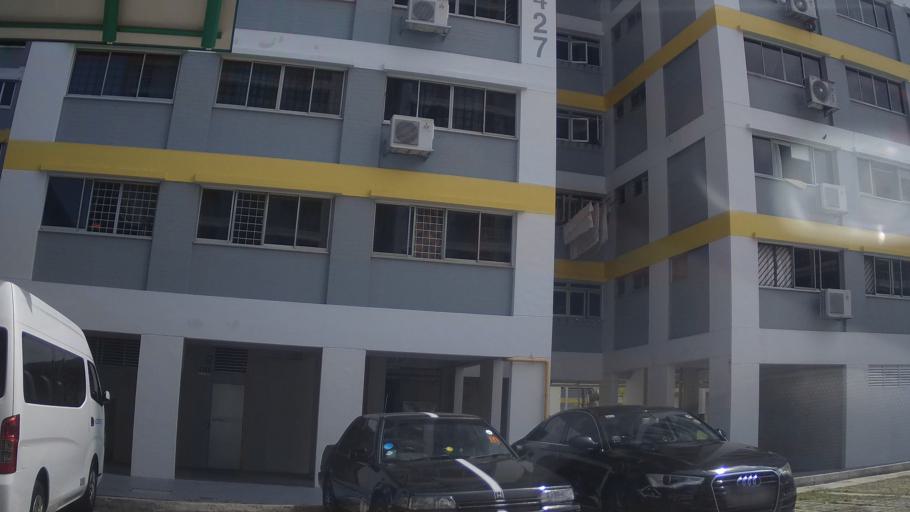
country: MY
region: Johor
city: Johor Bahru
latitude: 1.3861
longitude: 103.7696
